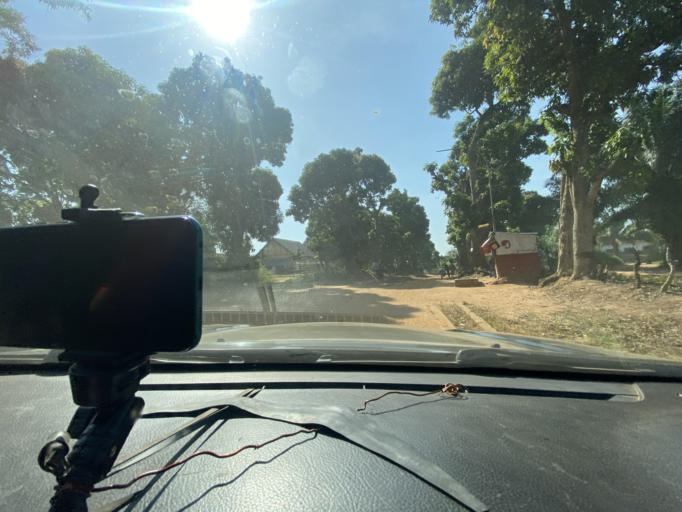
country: CD
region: Kasai-Oriental
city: Kabinda
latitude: -6.1302
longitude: 24.4937
